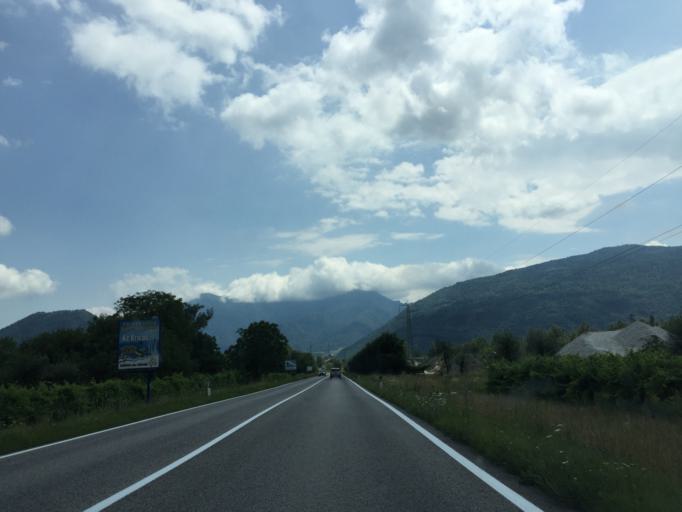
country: IT
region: Veneto
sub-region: Provincia di Belluno
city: Fonzaso
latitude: 46.0183
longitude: 11.7856
